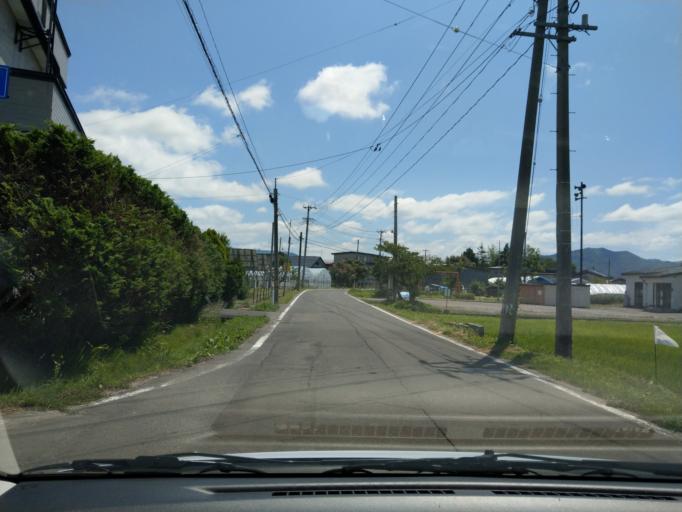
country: JP
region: Aomori
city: Kuroishi
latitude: 40.5762
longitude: 140.5518
